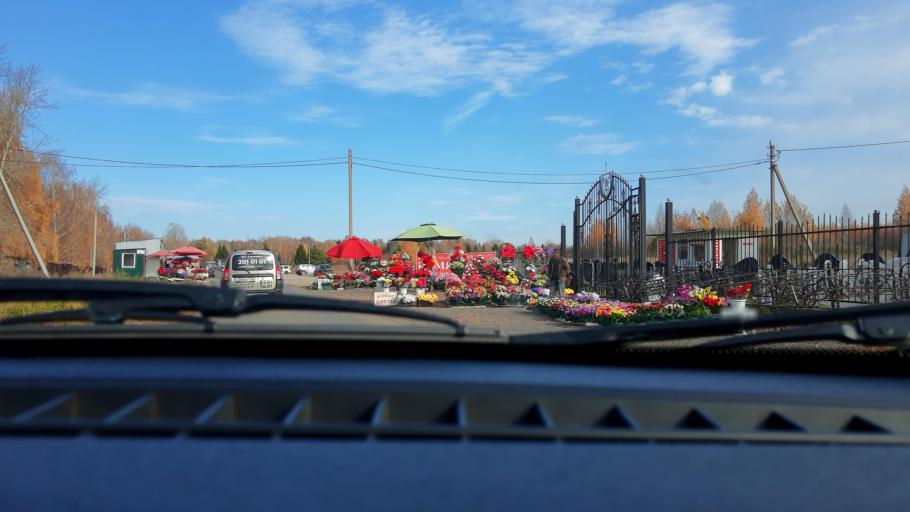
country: RU
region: Bashkortostan
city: Ufa
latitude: 54.8471
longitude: 56.1535
